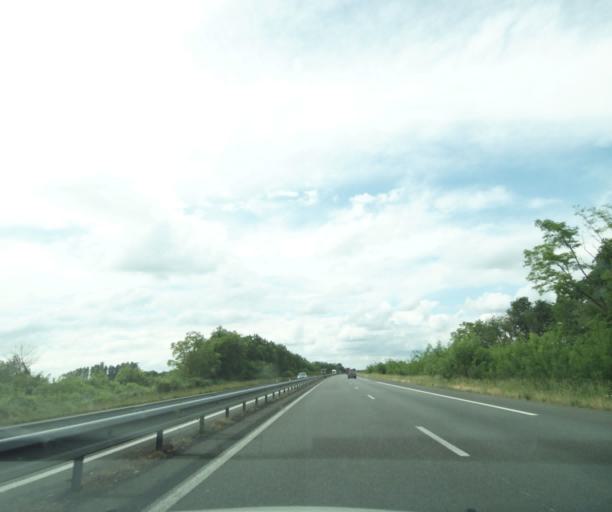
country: FR
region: Centre
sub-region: Departement du Cher
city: Mehun-sur-Yevre
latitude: 47.1158
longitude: 2.1979
